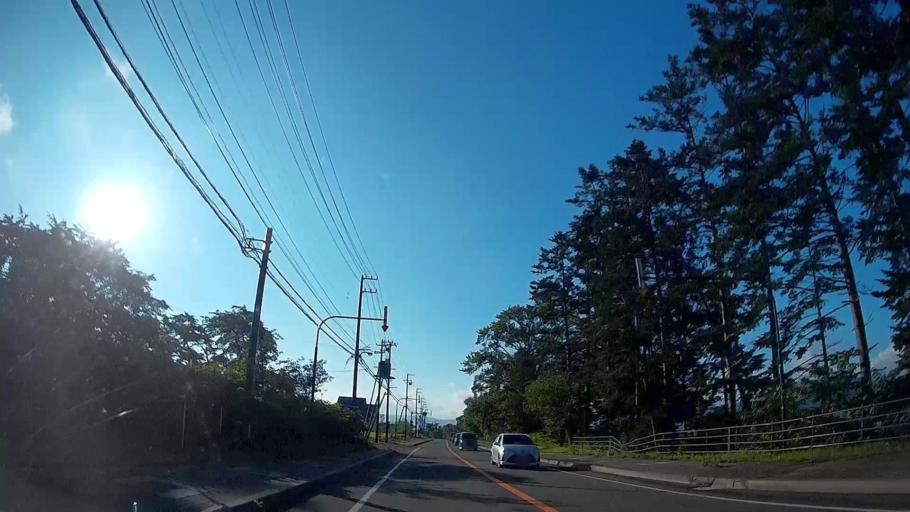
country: JP
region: Hokkaido
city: Date
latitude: 42.5575
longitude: 140.8554
